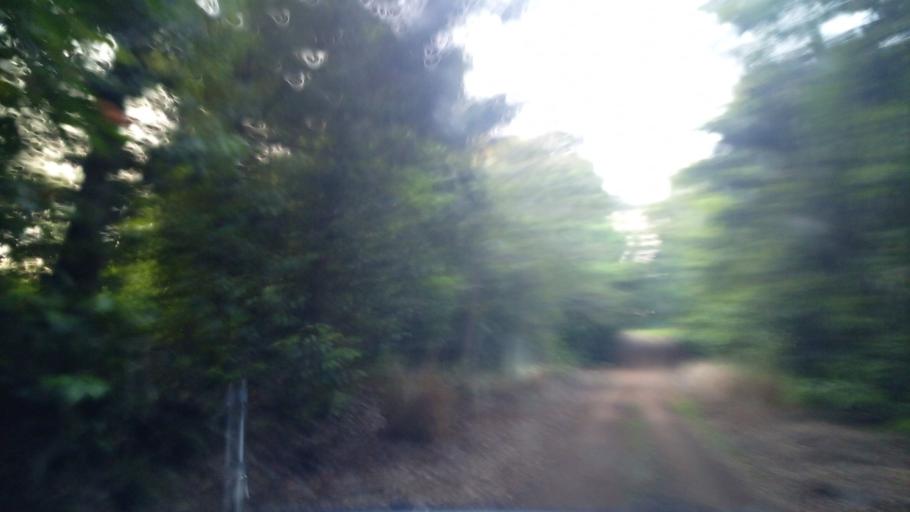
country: AU
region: Queensland
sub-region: Tablelands
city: Atherton
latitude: -17.3683
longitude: 145.7530
